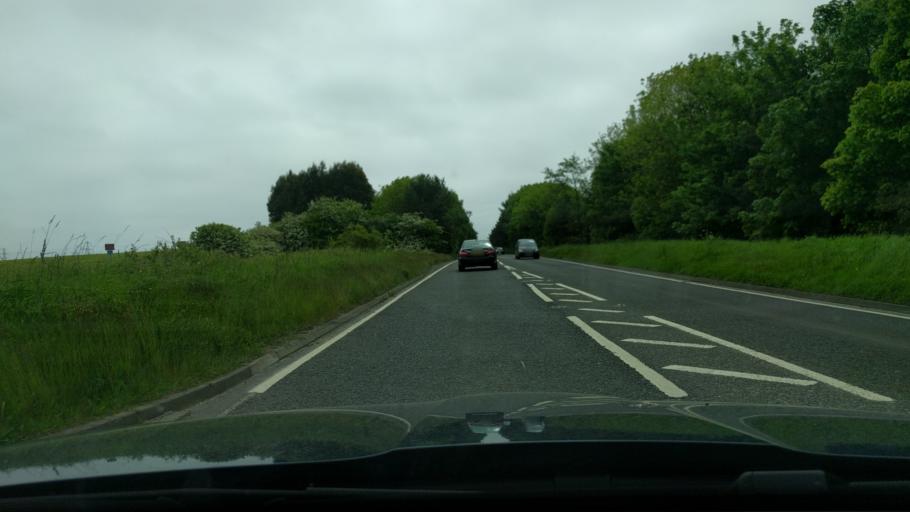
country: GB
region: England
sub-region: Northumberland
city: Lynemouth
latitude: 55.1957
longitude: -1.5486
